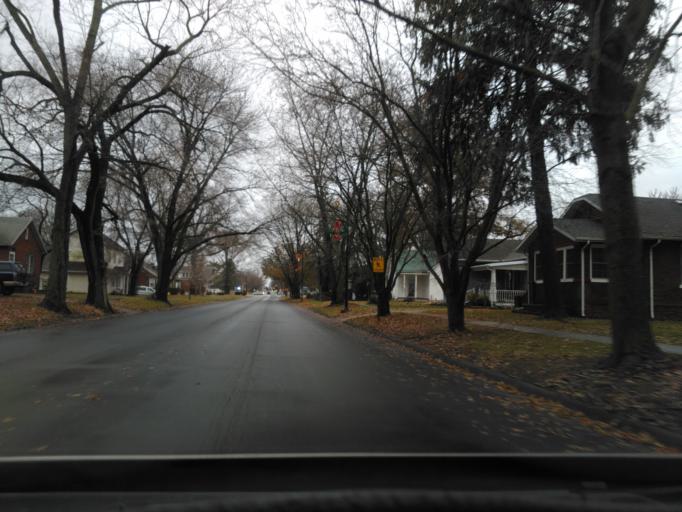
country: US
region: Illinois
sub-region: Effingham County
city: Altamont
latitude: 39.0575
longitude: -88.7480
